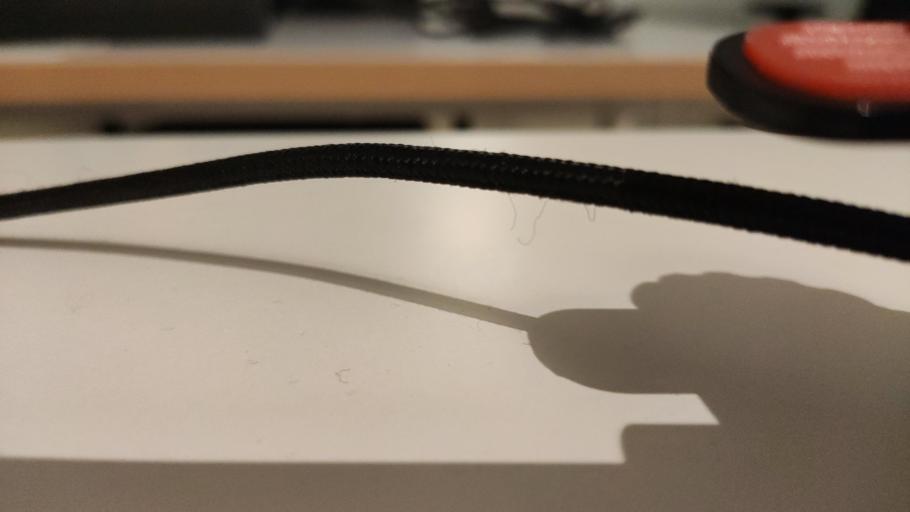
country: RU
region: Moskovskaya
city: Rogachevo
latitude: 56.4152
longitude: 37.2159
